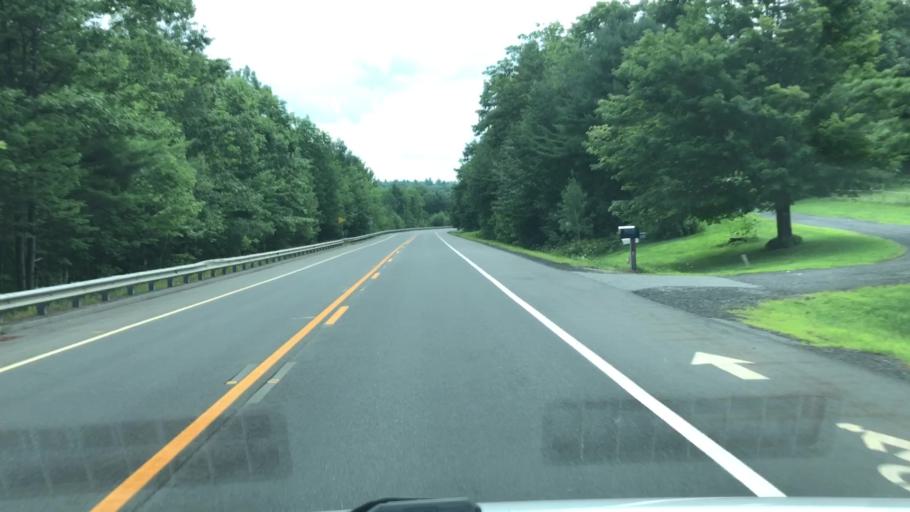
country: US
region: Massachusetts
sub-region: Franklin County
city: Ashfield
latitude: 42.4981
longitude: -72.8078
